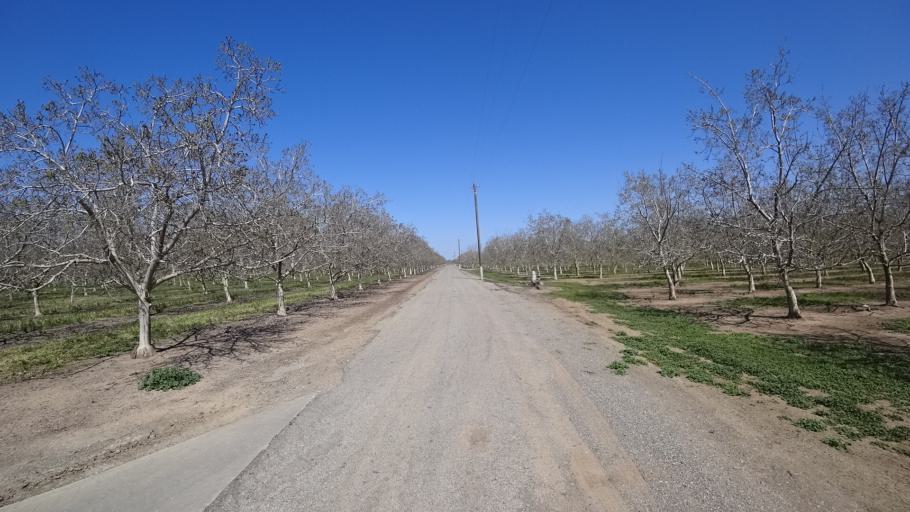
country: US
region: California
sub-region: Butte County
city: Biggs
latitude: 39.4603
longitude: -121.9396
